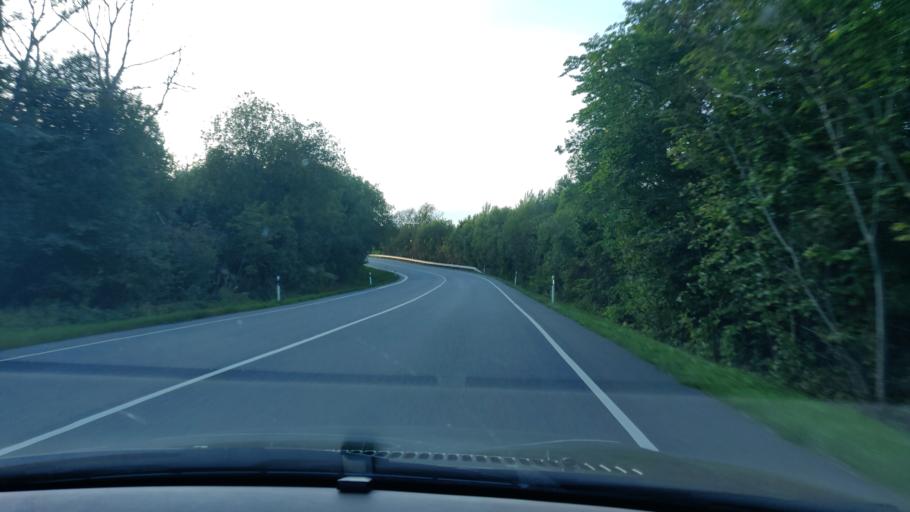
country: EE
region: Harju
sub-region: Keila linn
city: Keila
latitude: 59.4207
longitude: 24.3342
